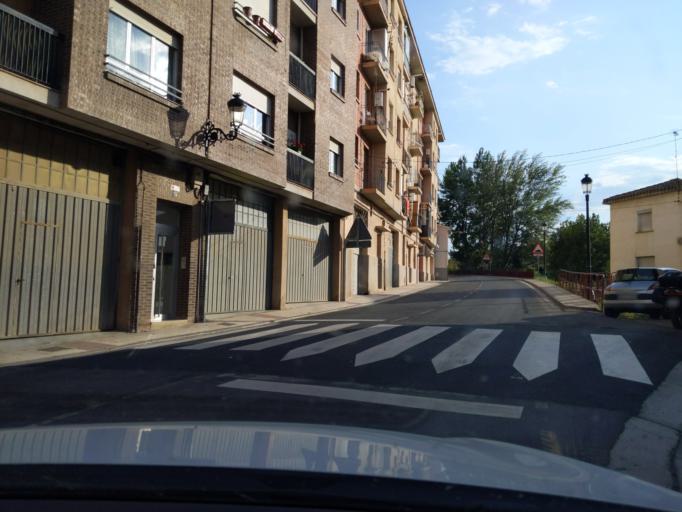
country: ES
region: La Rioja
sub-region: Provincia de La Rioja
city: Albelda de Iregua
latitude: 42.3560
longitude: -2.4738
